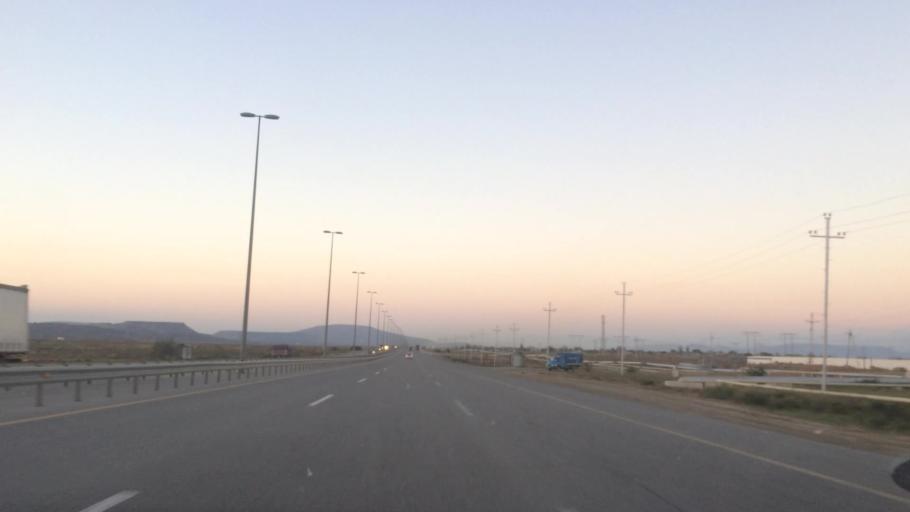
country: AZ
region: Baki
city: Qobustan
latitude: 40.0025
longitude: 49.4297
